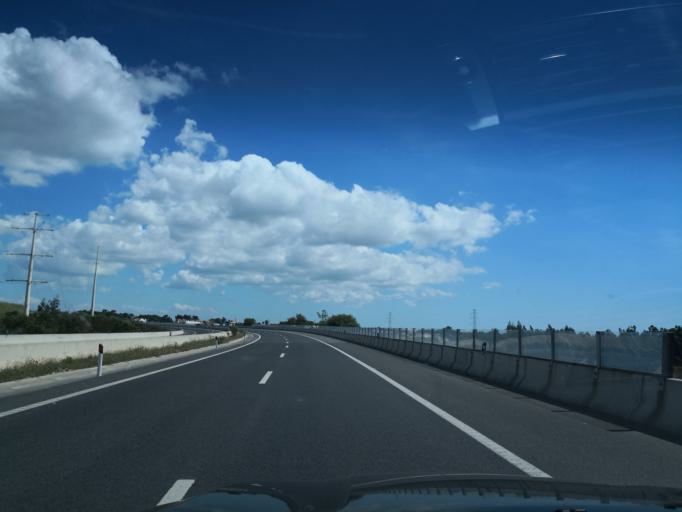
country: PT
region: Setubal
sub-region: Almada
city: Charneca
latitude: 38.6128
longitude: -9.1680
